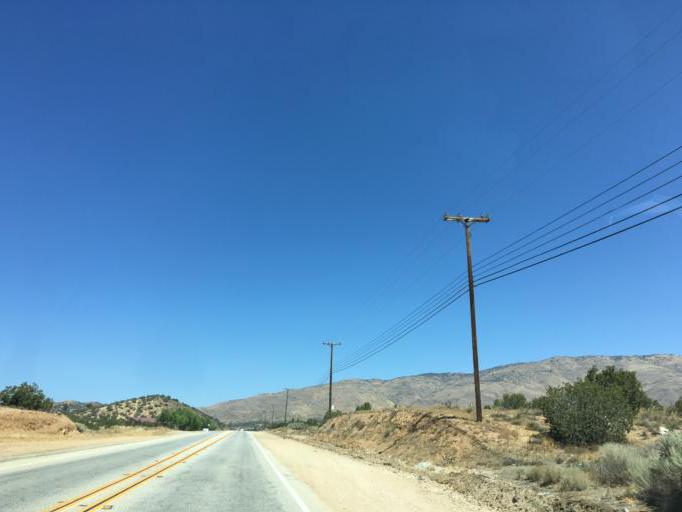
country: US
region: California
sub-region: Los Angeles County
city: Acton
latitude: 34.5072
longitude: -118.2322
